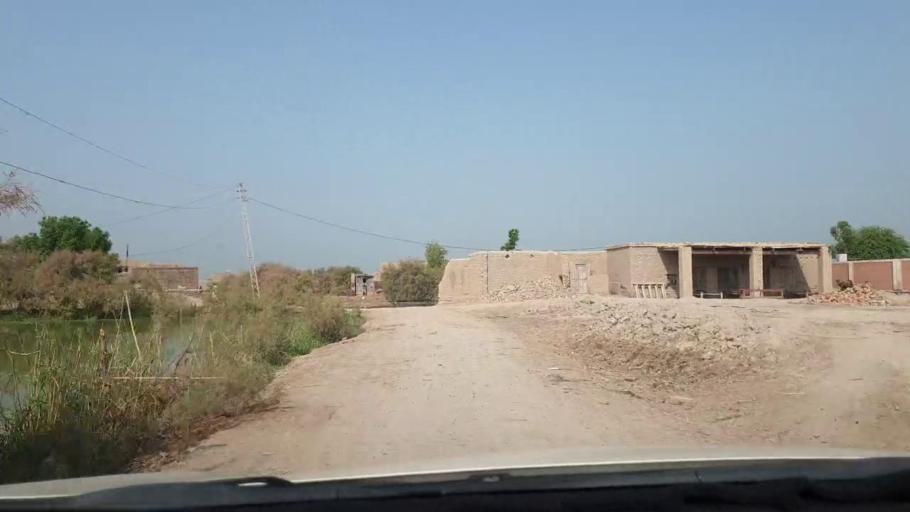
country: PK
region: Sindh
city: Goth Garelo
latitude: 27.4584
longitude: 68.1205
